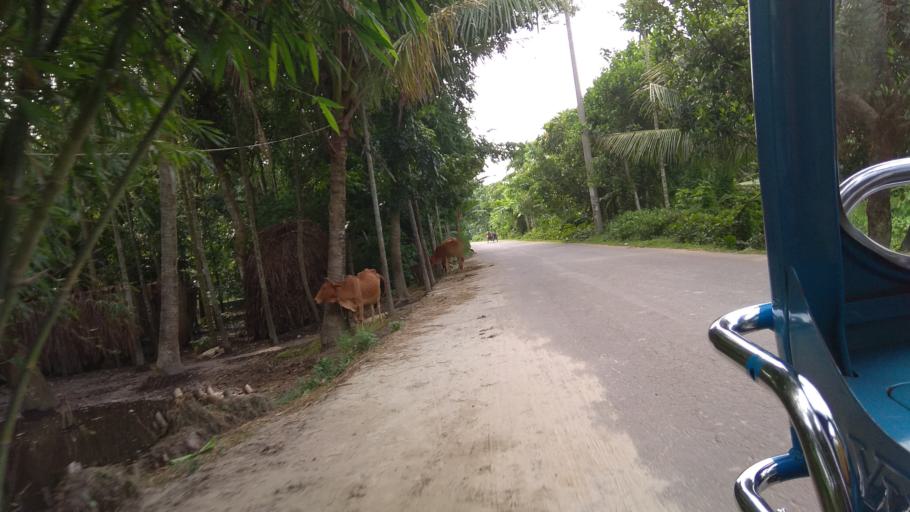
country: BD
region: Dhaka
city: Tungipara
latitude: 22.9924
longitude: 89.7806
